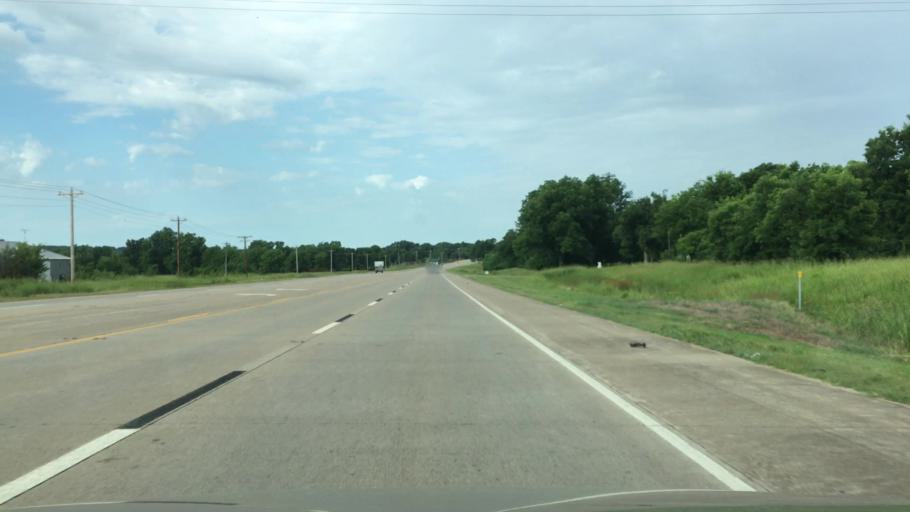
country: US
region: Oklahoma
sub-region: Cherokee County
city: Park Hill
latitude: 35.8245
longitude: -95.0494
